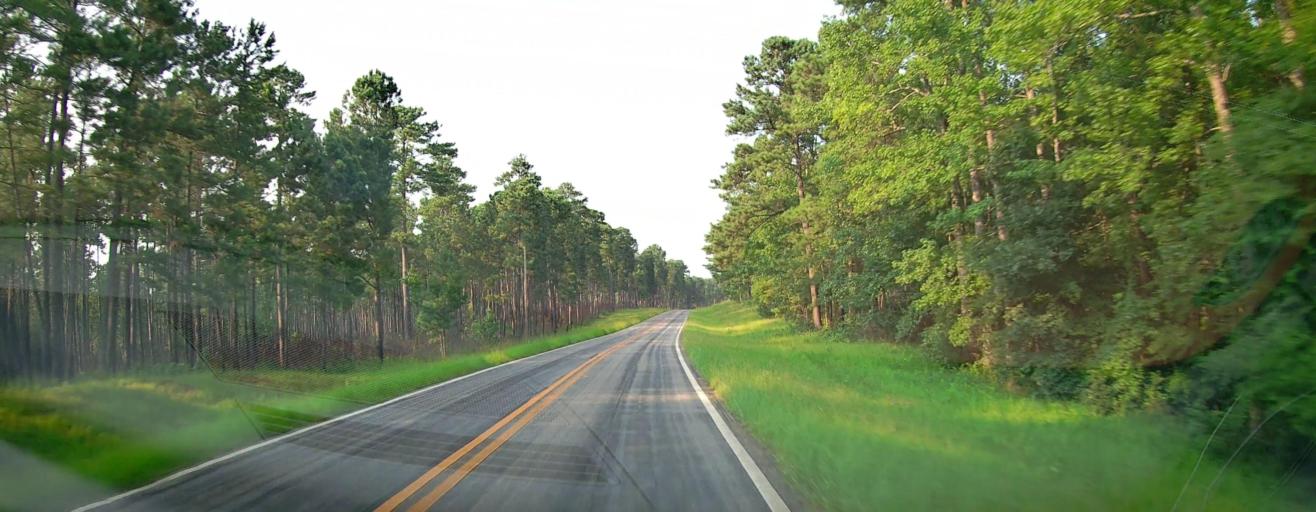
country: US
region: Georgia
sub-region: Jones County
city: Gray
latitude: 33.1090
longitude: -83.6590
